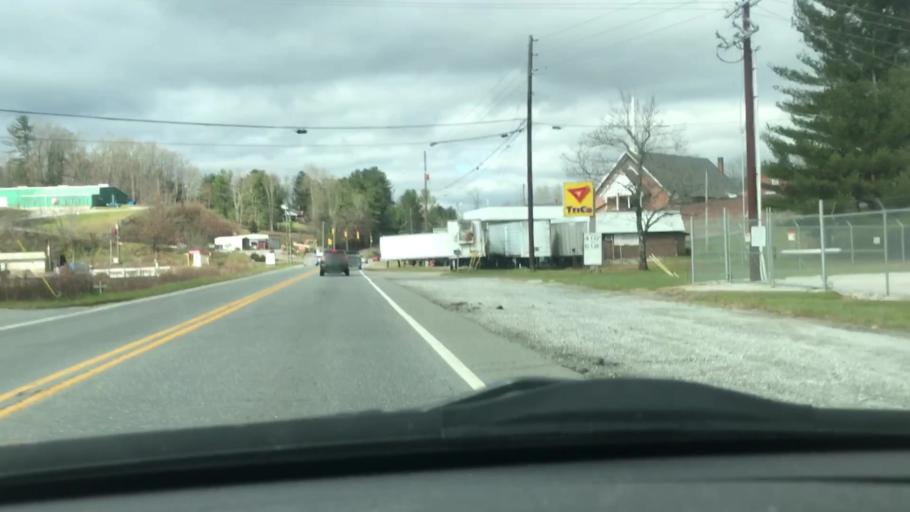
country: US
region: North Carolina
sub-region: Mitchell County
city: Spruce Pine
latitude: 35.8809
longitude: -82.0561
